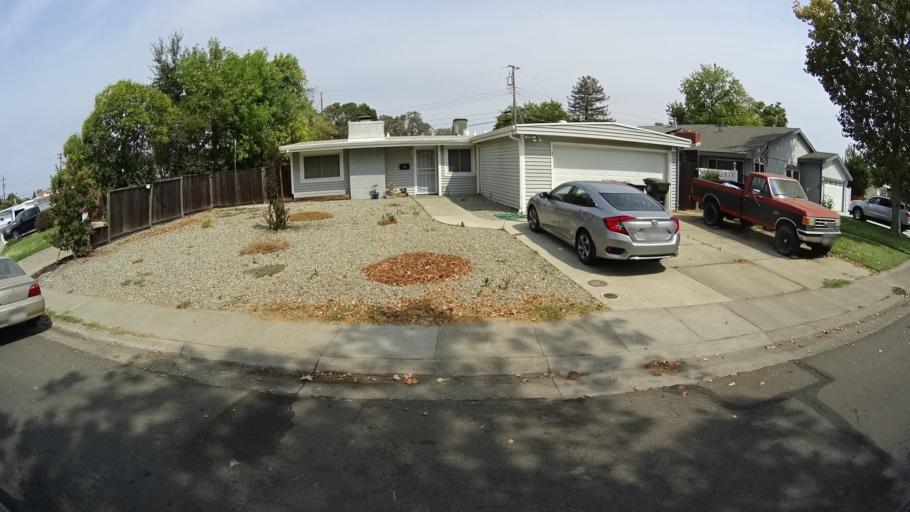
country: US
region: California
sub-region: Sacramento County
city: Elk Grove
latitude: 38.4191
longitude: -121.3725
